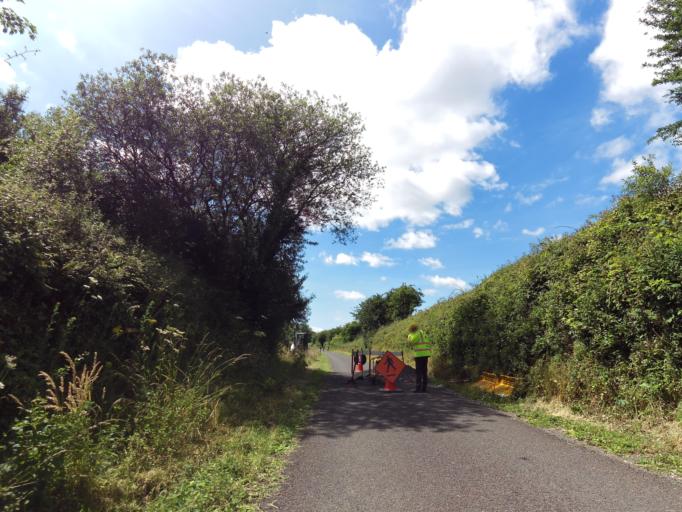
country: IE
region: Leinster
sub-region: Kilkenny
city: Mooncoin
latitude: 52.2461
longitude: -7.2562
